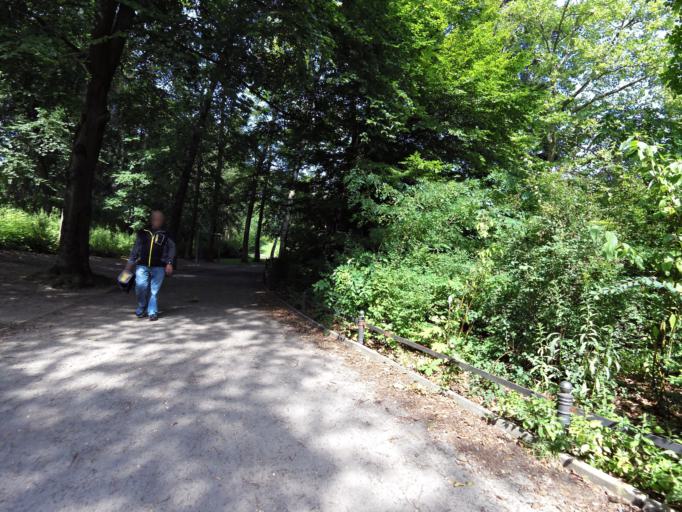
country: DE
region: Berlin
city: Lankwitz
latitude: 52.4304
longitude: 13.3515
